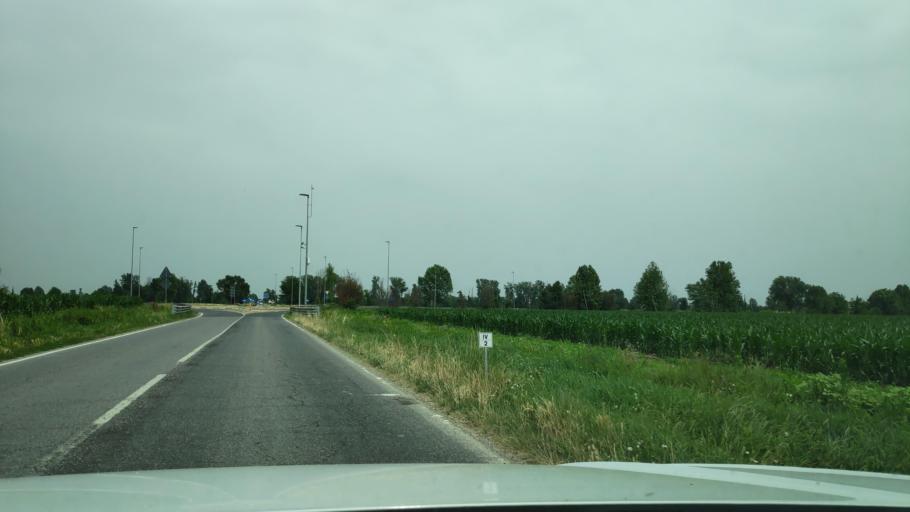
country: IT
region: Lombardy
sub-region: Provincia di Cremona
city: Campagnola Cremasca
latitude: 45.4071
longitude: 9.6589
